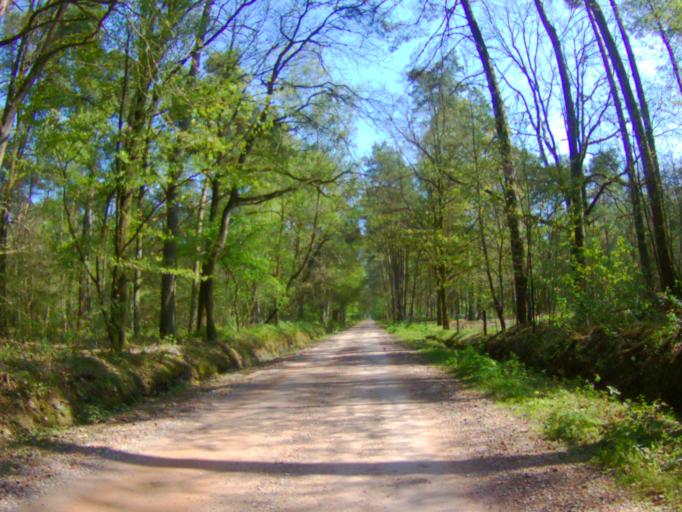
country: BE
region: Flanders
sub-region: Provincie Antwerpen
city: Brecht
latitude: 51.3118
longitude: 4.5867
